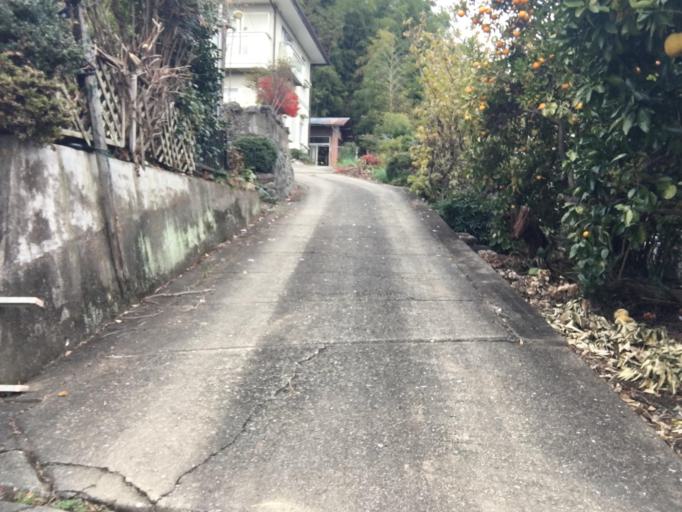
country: JP
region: Saitama
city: Yorii
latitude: 36.1344
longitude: 139.1990
